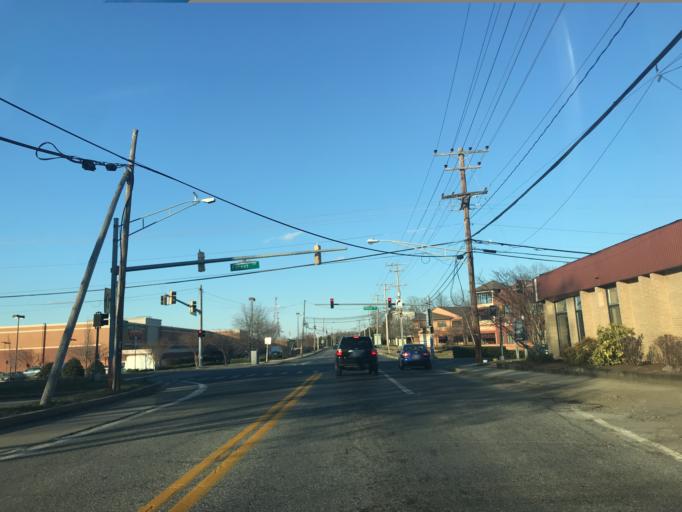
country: US
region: Maryland
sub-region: Anne Arundel County
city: Parole
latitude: 38.9776
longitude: -76.5376
